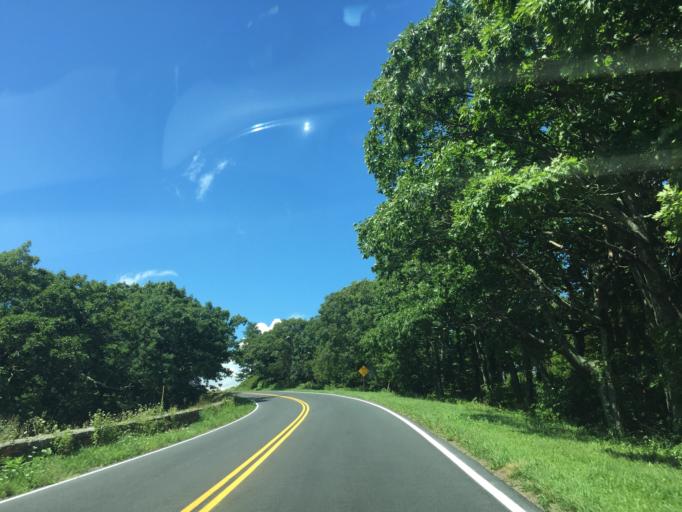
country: US
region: Virginia
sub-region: Rappahannock County
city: Washington
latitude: 38.7614
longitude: -78.2767
